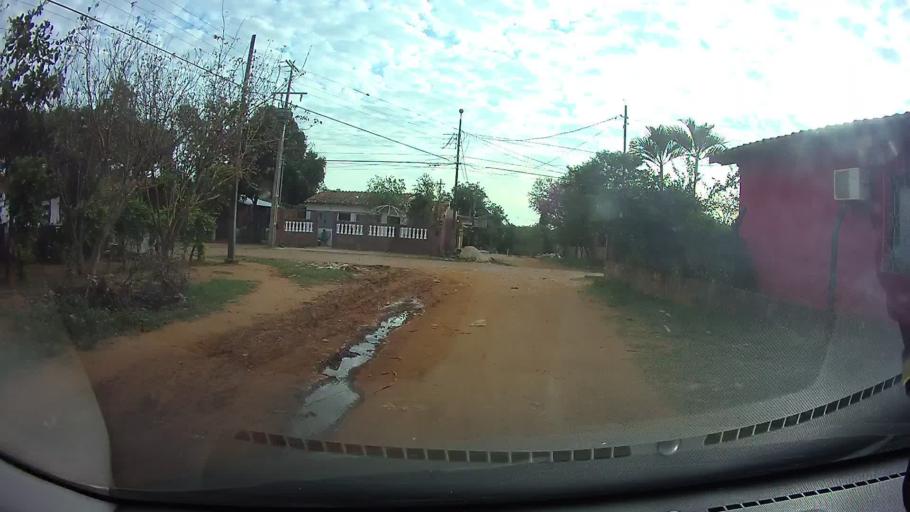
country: PY
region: Central
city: Limpio
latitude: -25.2511
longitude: -57.5053
